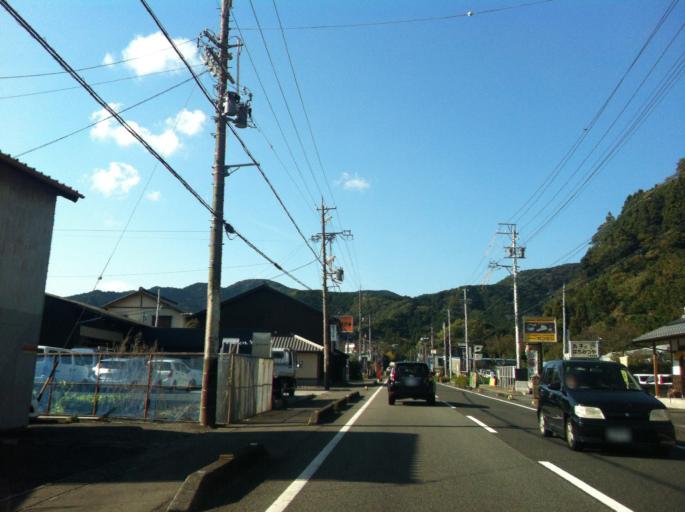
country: JP
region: Shizuoka
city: Shizuoka-shi
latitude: 34.9506
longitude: 138.3397
